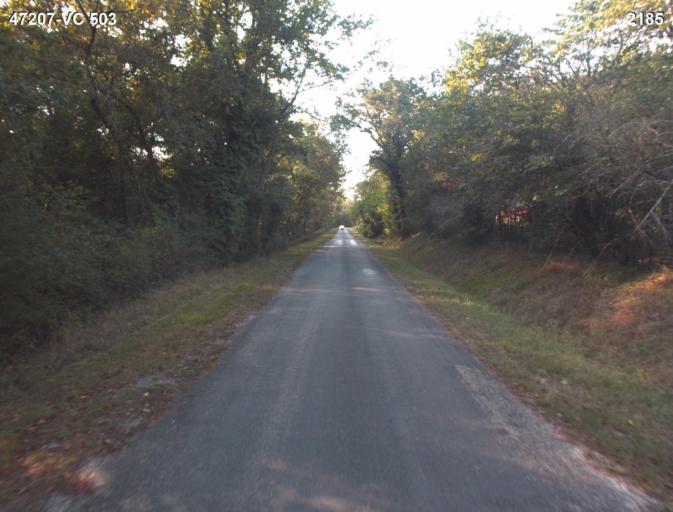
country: FR
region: Aquitaine
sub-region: Departement du Lot-et-Garonne
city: Barbaste
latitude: 44.1892
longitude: 0.2331
